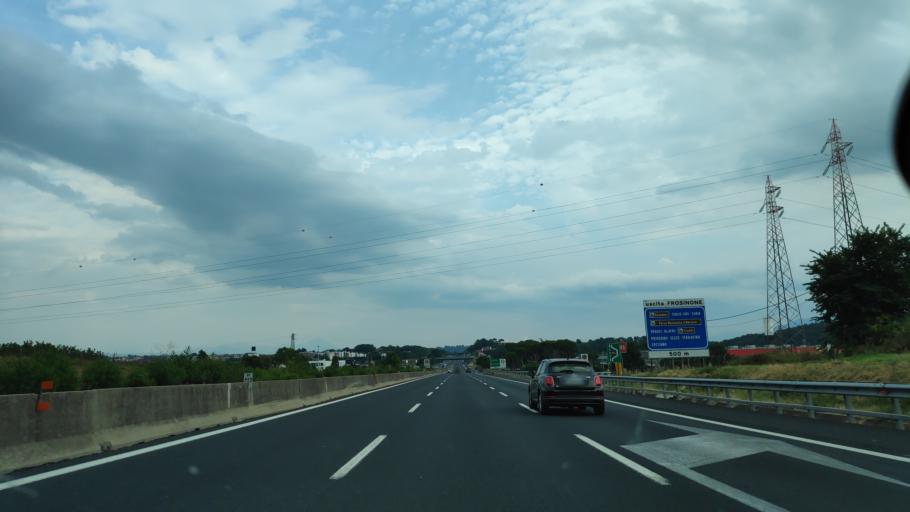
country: IT
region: Latium
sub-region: Provincia di Frosinone
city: Frosinone
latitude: 41.6227
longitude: 13.3034
